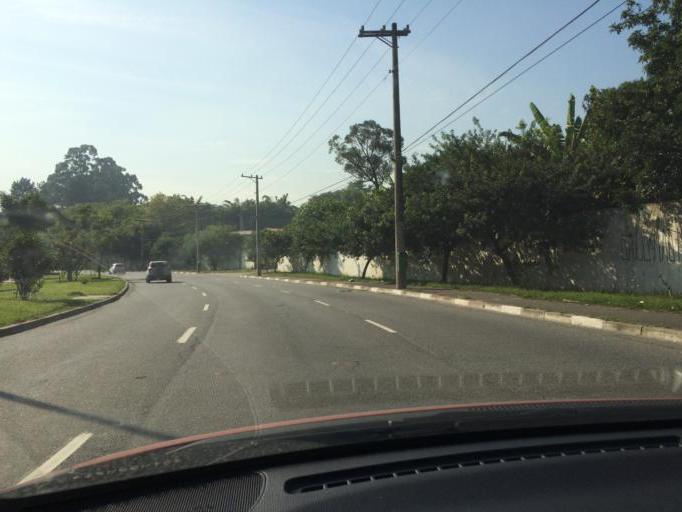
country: BR
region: Sao Paulo
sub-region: Osasco
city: Osasco
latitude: -23.5587
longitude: -46.7443
